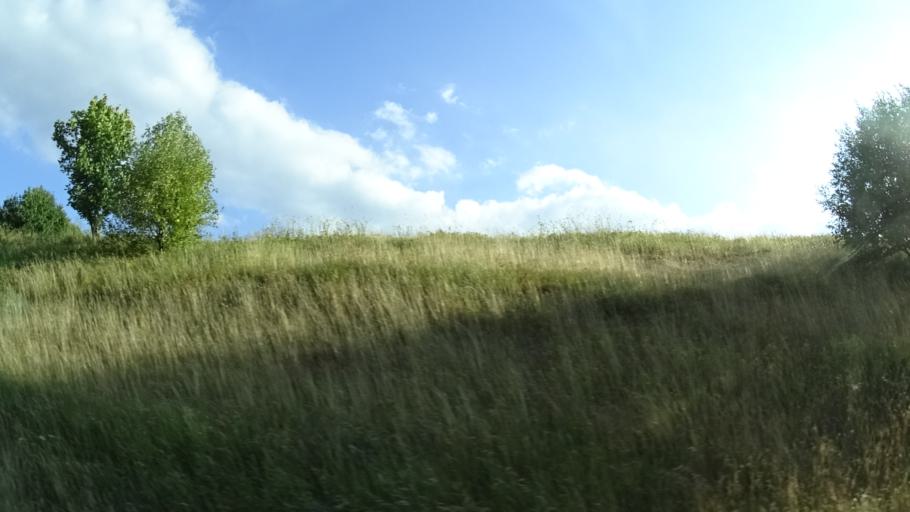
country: DE
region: Bavaria
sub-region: Regierungsbezirk Unterfranken
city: Wildflecken
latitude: 50.4052
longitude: 9.9500
